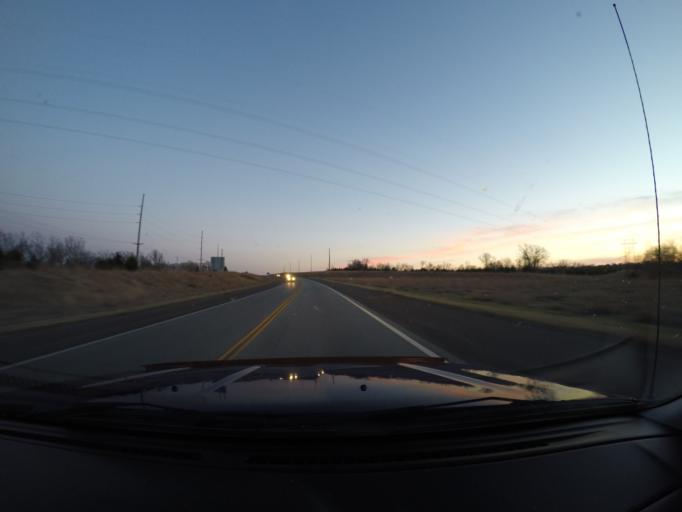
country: US
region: Kansas
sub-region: Douglas County
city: Lawrence
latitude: 38.9888
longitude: -95.3425
